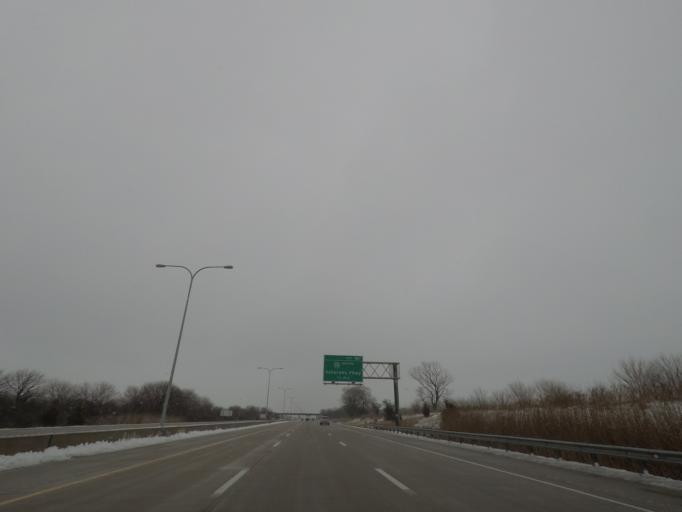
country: US
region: Illinois
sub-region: McLean County
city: Normal
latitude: 40.5387
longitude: -88.9688
